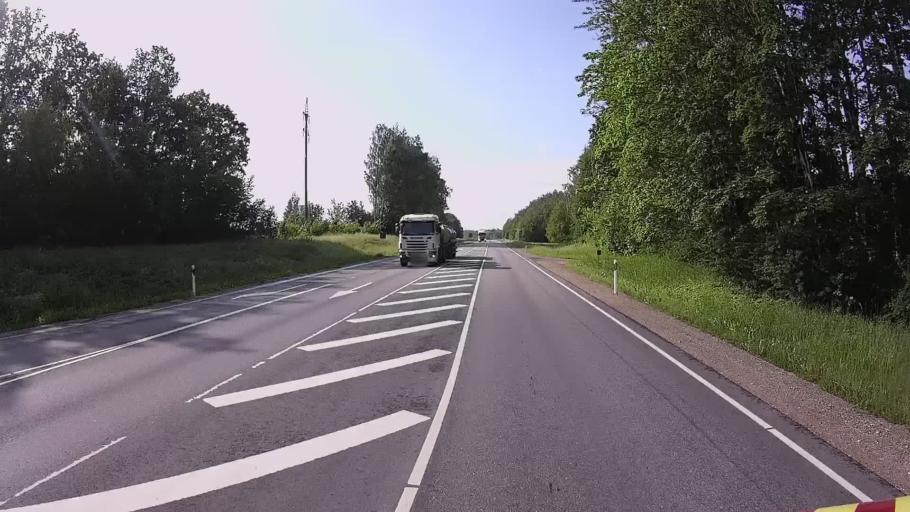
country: EE
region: Viljandimaa
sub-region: Viljandi linn
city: Viljandi
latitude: 58.3454
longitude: 25.5650
